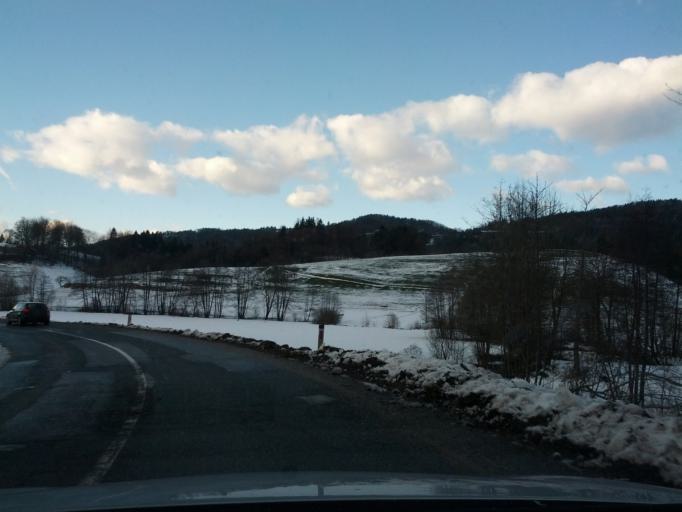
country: SI
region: Moravce
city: Moravce
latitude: 46.1381
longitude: 14.8033
